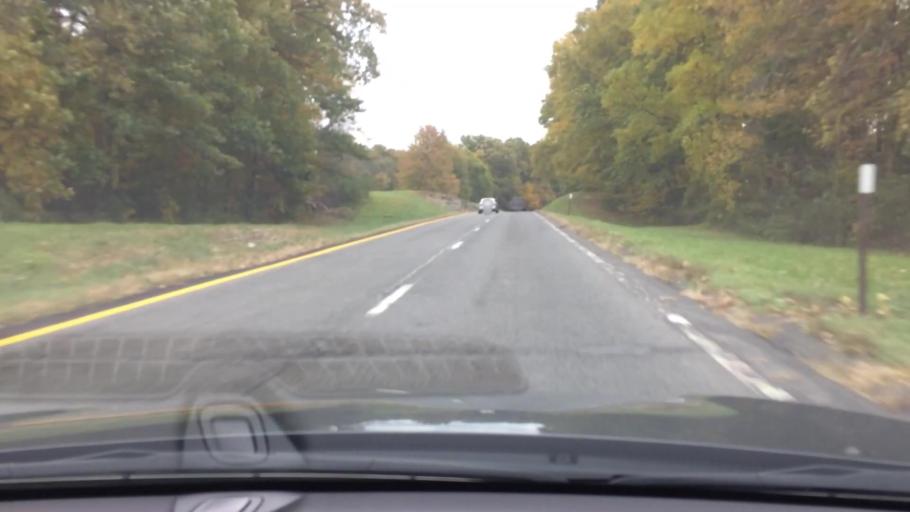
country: US
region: New York
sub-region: Dutchess County
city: Hillside Lake
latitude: 41.6400
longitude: -73.7858
